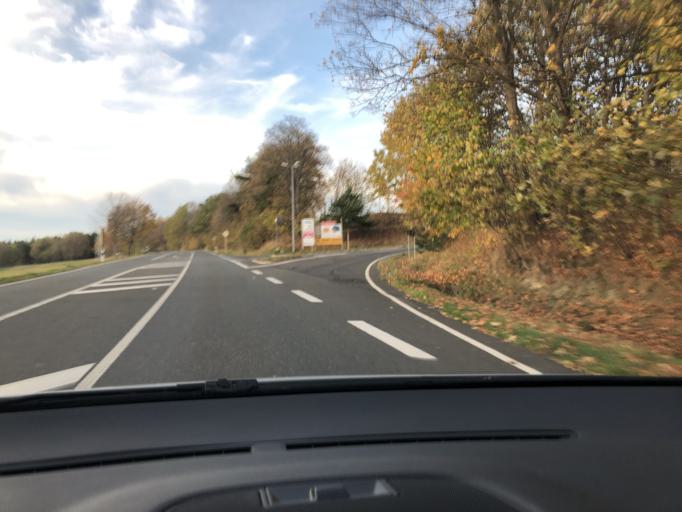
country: DE
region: Thuringia
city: Martinroda
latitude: 50.7001
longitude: 10.8959
